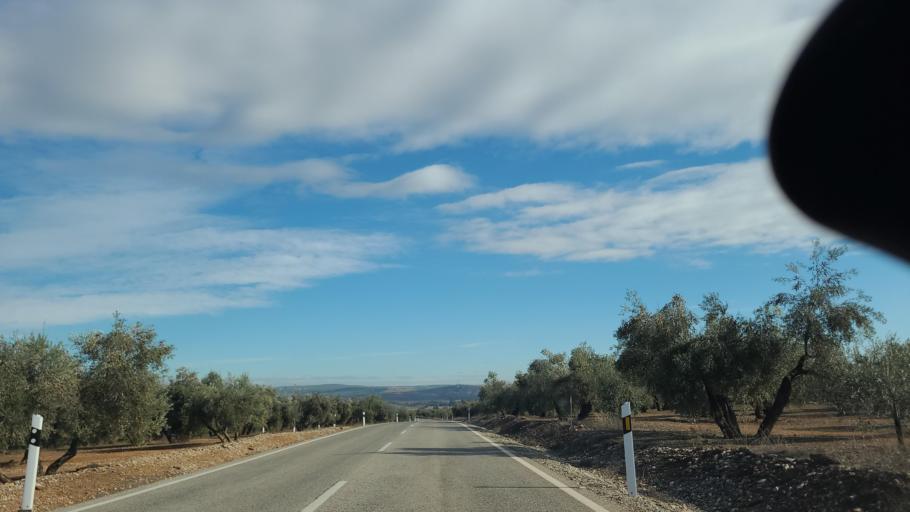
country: ES
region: Andalusia
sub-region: Provincia de Jaen
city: Espeluy
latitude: 38.0238
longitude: -3.8568
